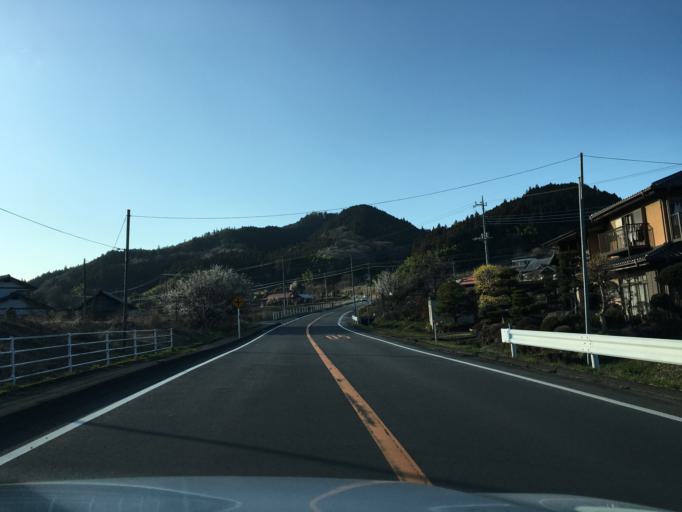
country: JP
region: Ibaraki
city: Daigo
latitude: 36.7789
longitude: 140.2750
